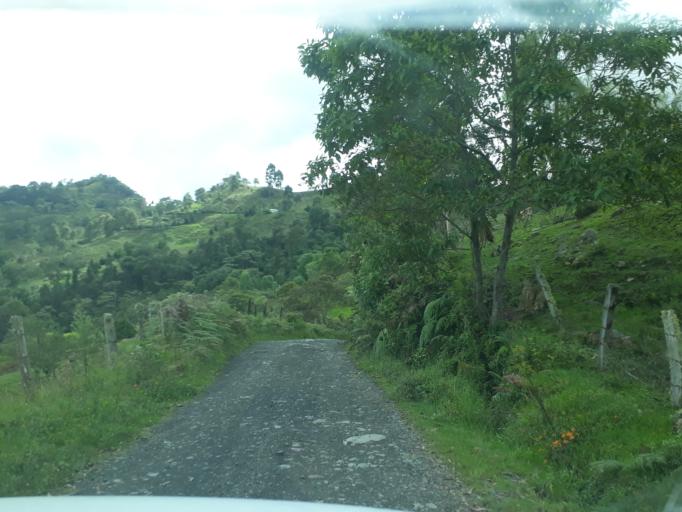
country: CO
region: Cundinamarca
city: Carmen de Carupa
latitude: 5.3486
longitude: -74.0607
